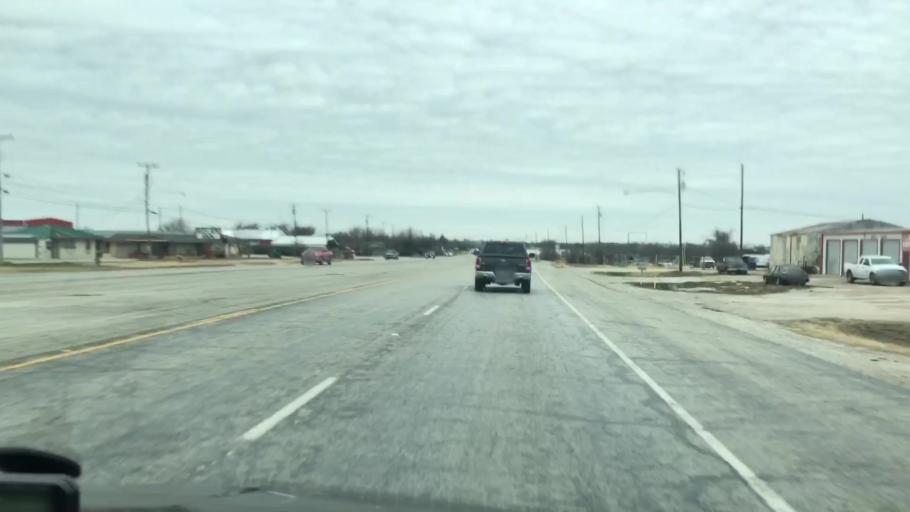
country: US
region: Texas
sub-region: Jack County
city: Jacksboro
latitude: 33.2030
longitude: -98.1512
